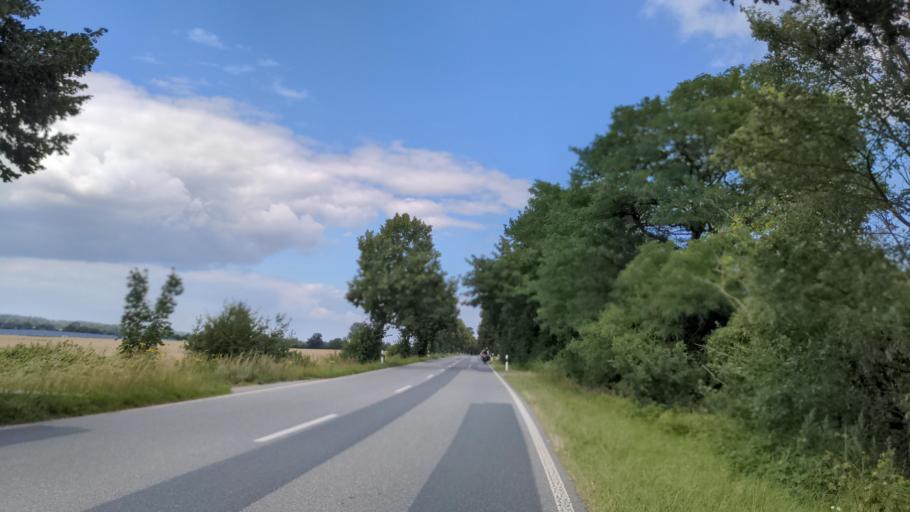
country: DE
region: Schleswig-Holstein
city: Beschendorf
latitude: 54.1693
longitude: 10.8736
